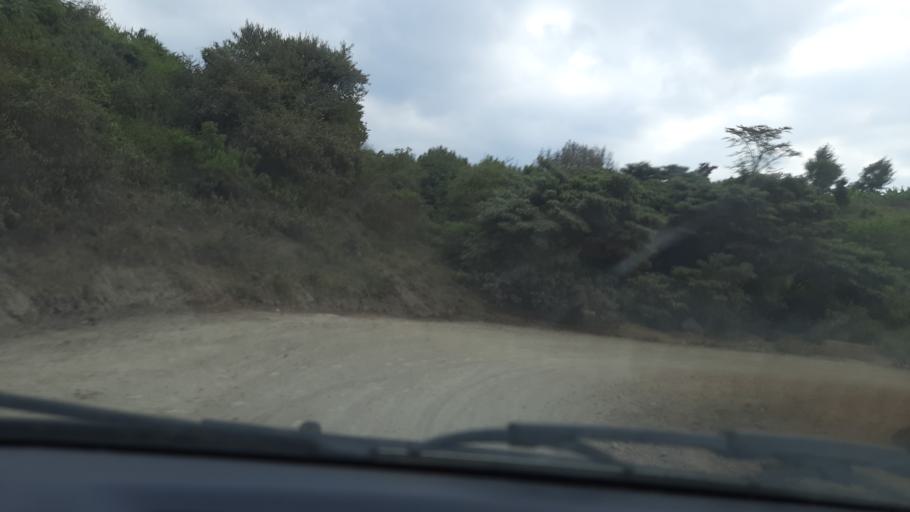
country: TZ
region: Kilimanjaro
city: Moshi
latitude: -2.8698
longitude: 37.3310
